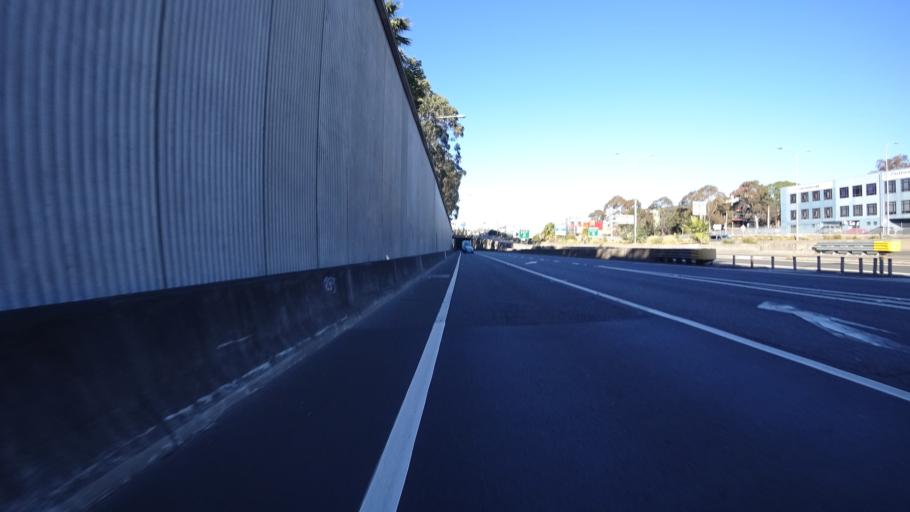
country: AU
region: New South Wales
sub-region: Willoughby
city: Artarmon
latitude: -33.8128
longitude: 151.1830
